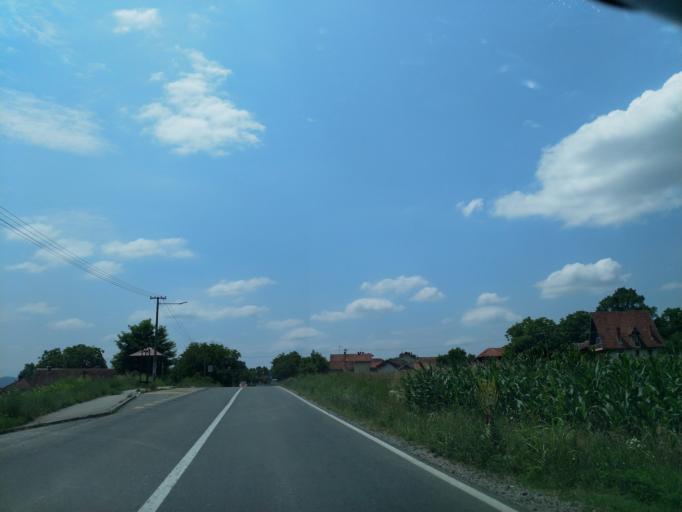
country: RS
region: Central Serbia
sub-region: Rasinski Okrug
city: Krusevac
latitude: 43.4958
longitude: 21.2867
